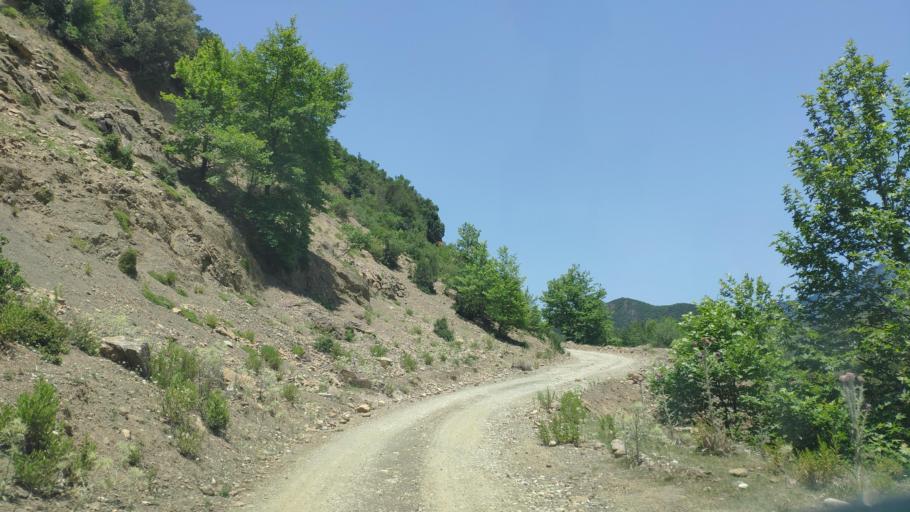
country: GR
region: Thessaly
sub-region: Nomos Kardhitsas
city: Anthiro
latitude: 39.1734
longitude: 21.3701
